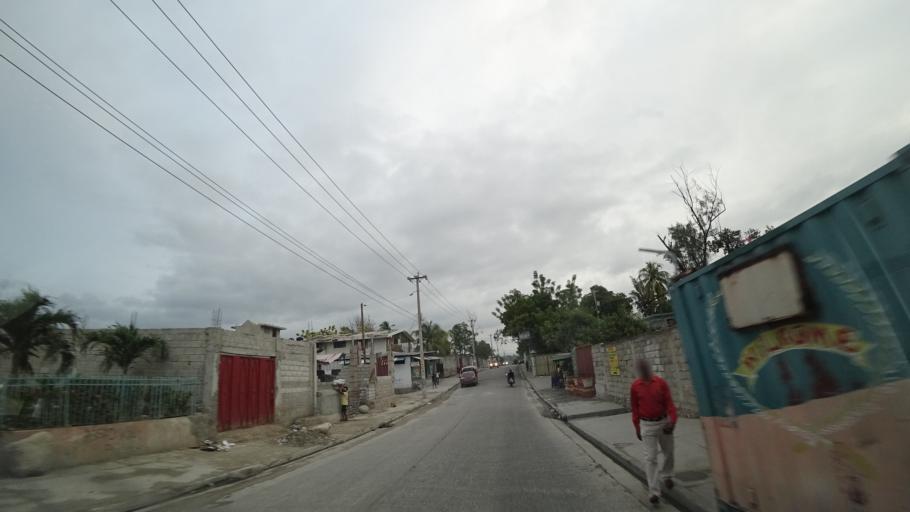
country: HT
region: Ouest
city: Delmas 73
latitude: 18.5575
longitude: -72.3030
